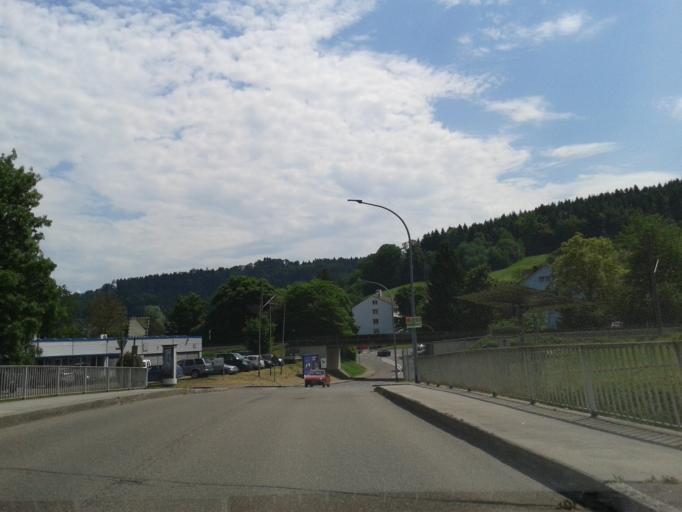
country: DE
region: Baden-Wuerttemberg
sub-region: Regierungsbezirk Stuttgart
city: Murrhardt
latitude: 48.9861
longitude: 9.5538
